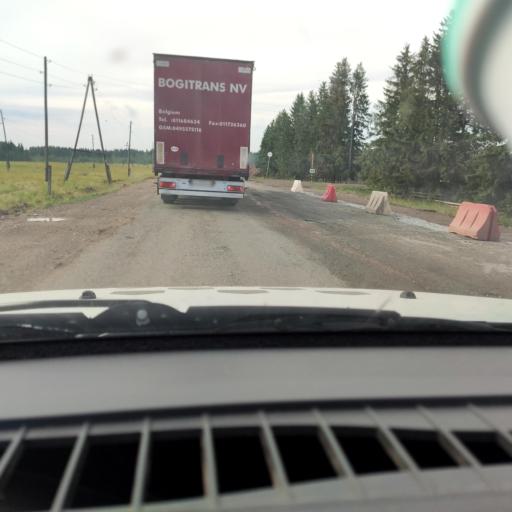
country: RU
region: Kirov
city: Kostino
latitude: 58.8265
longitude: 53.3095
